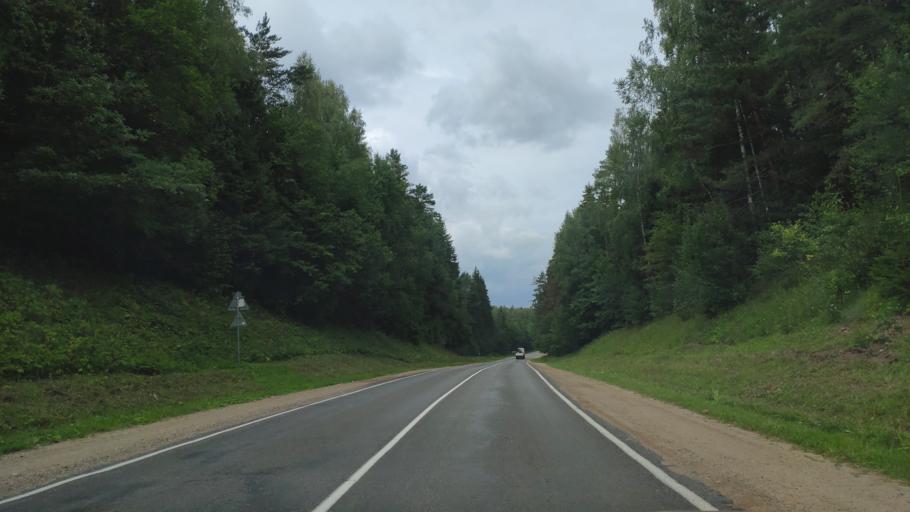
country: BY
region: Minsk
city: Novosel'ye
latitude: 53.9282
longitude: 27.2439
